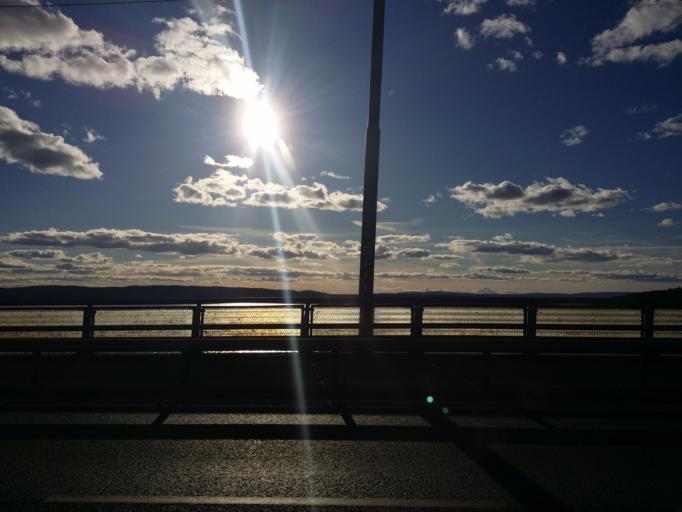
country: NO
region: Akershus
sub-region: Oppegard
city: Kolbotn
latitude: 59.8581
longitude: 10.7843
